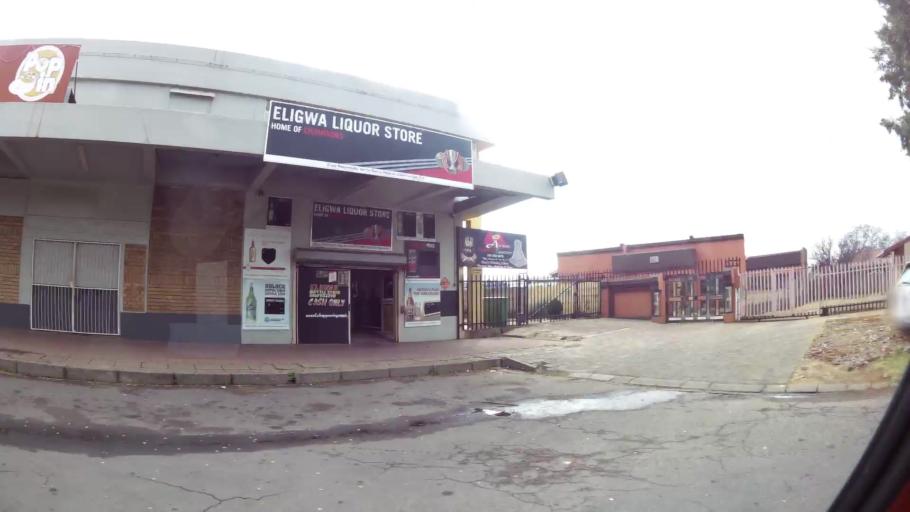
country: ZA
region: Gauteng
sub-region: Sedibeng District Municipality
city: Vanderbijlpark
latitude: -26.6803
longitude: 27.8332
